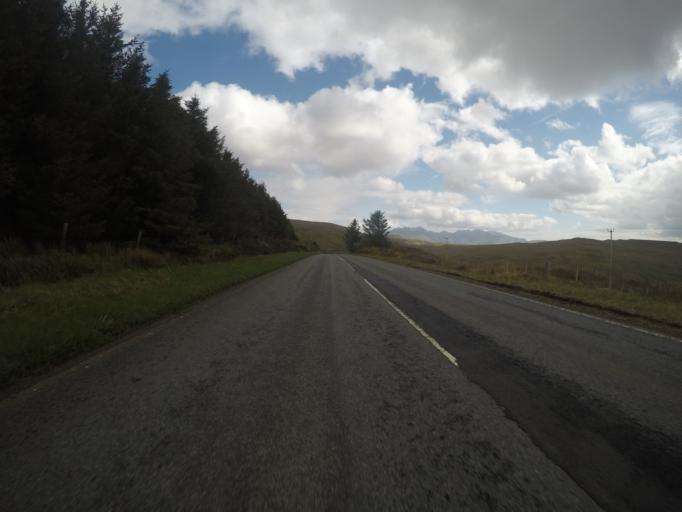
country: GB
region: Scotland
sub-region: Highland
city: Isle of Skye
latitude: 57.3321
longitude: -6.3450
